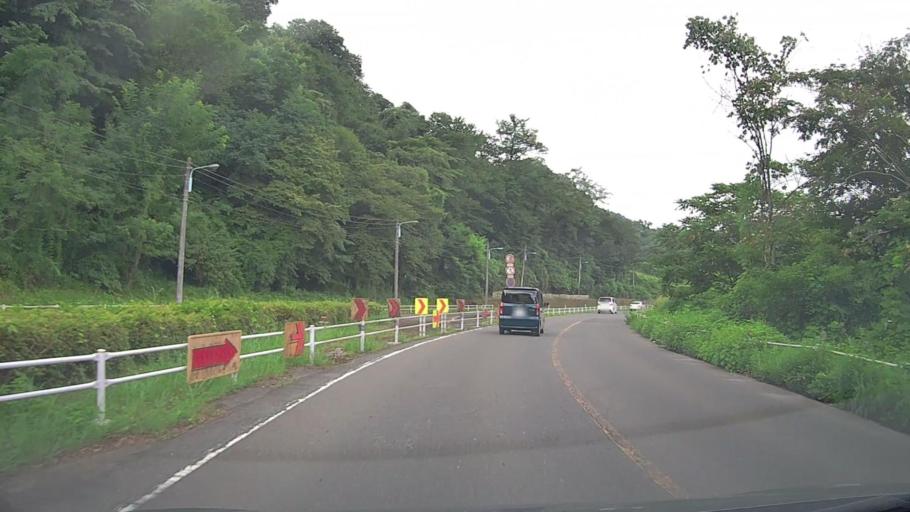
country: JP
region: Tokyo
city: Itsukaichi
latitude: 35.7162
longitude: 139.2682
